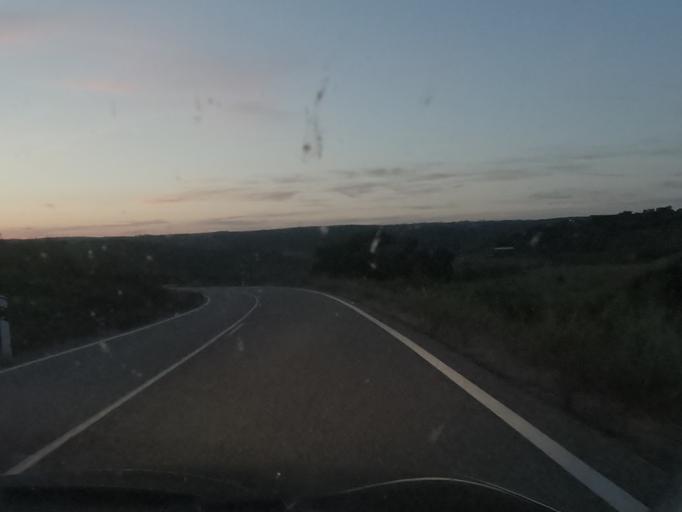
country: ES
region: Extremadura
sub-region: Provincia de Caceres
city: Piedras Albas
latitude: 39.8056
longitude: -6.9746
